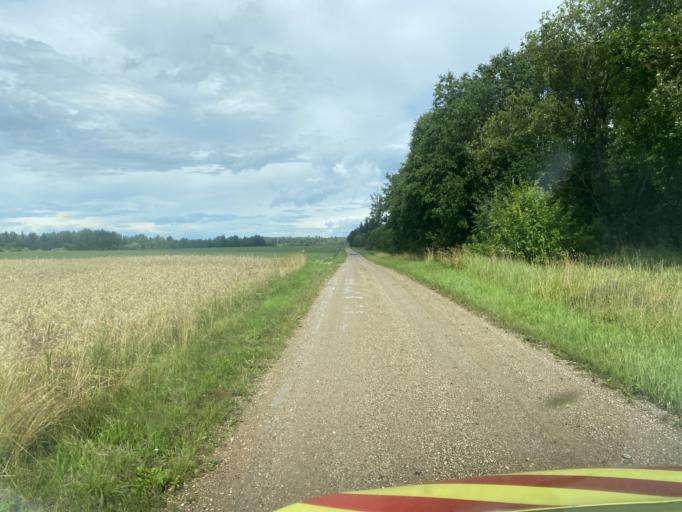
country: EE
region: Valgamaa
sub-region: Torva linn
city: Torva
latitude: 58.0993
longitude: 26.0022
